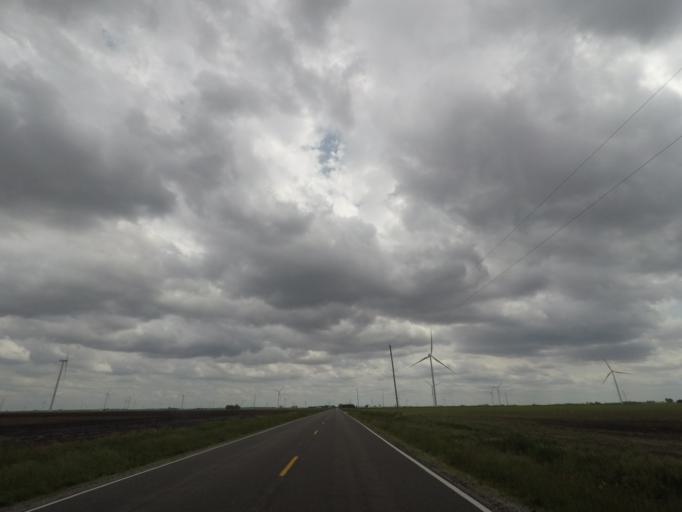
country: US
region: Illinois
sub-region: Macon County
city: Warrensburg
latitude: 40.0177
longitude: -89.0856
